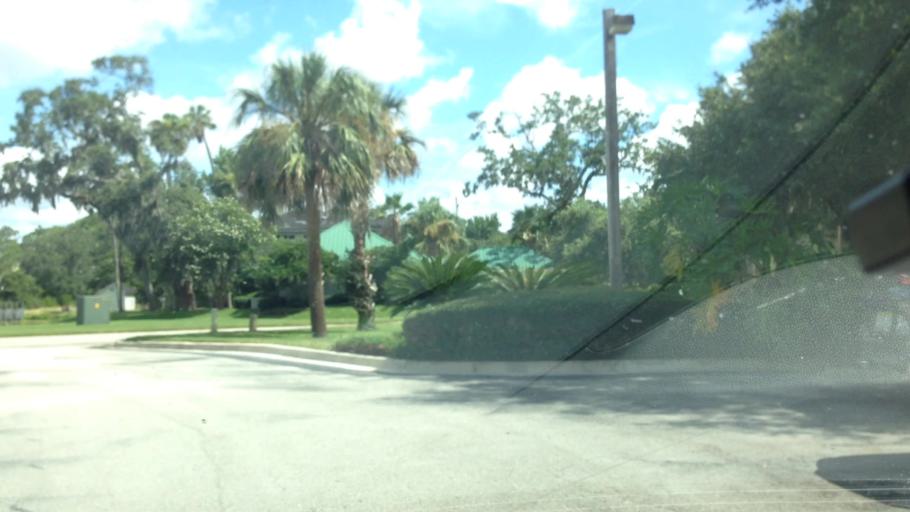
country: US
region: Florida
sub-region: Saint Johns County
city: Ponte Vedra Beach
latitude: 30.2533
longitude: -81.4016
